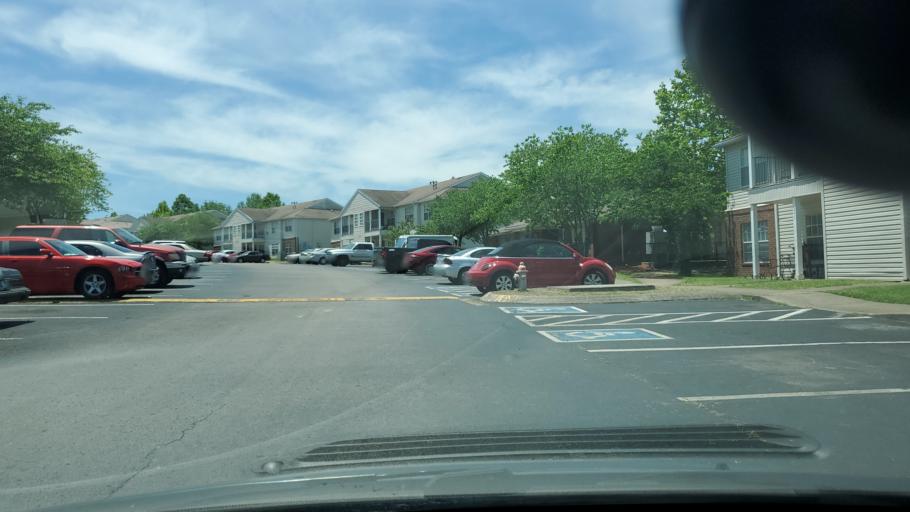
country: US
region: Tennessee
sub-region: Davidson County
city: Nashville
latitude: 36.2245
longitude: -86.7446
